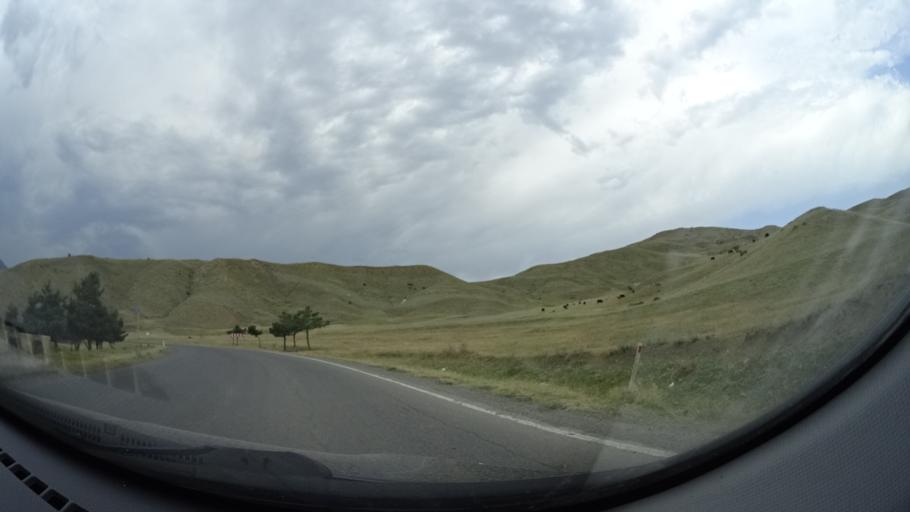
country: GE
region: Samtskhe-Javakheti
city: Aspindza
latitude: 41.5976
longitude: 43.1946
